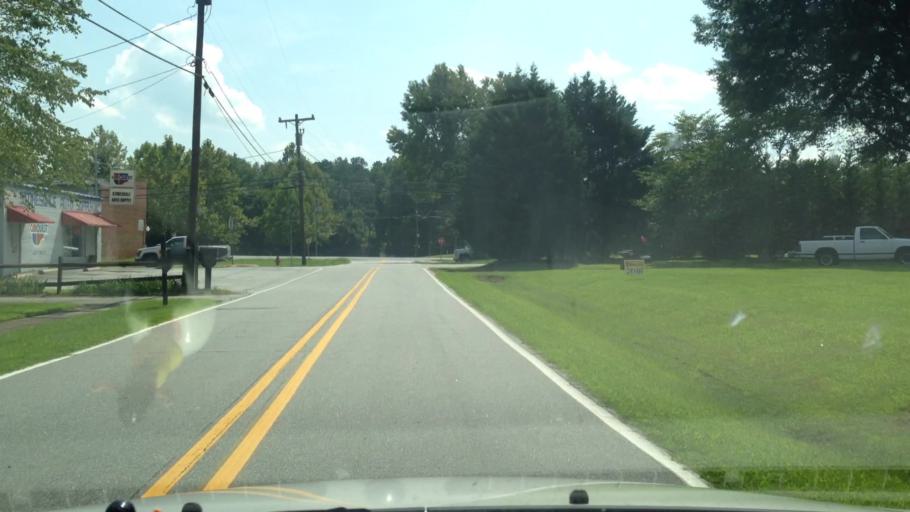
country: US
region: North Carolina
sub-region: Guilford County
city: Stokesdale
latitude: 36.2430
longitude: -79.9840
